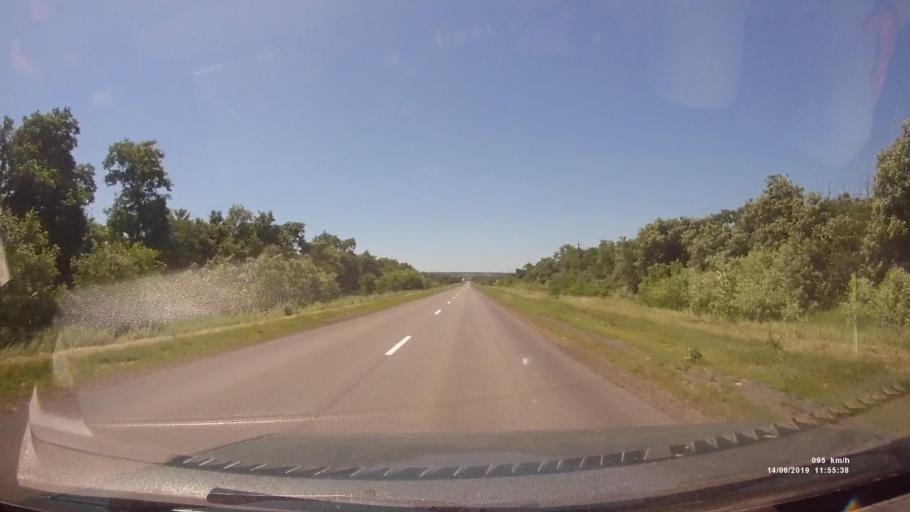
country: RU
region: Rostov
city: Kazanskaya
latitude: 49.8088
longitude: 41.1735
